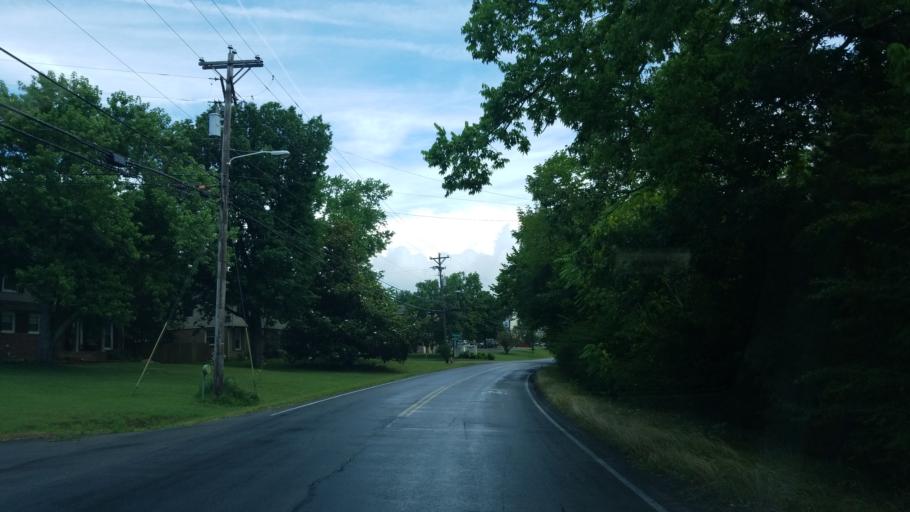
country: US
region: Tennessee
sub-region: Rutherford County
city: La Vergne
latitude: 36.1017
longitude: -86.6039
